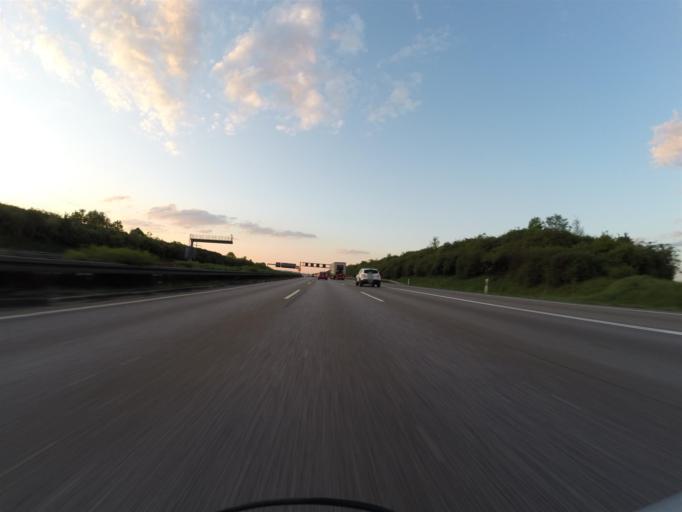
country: DE
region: Hesse
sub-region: Regierungsbezirk Darmstadt
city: Friedrichsdorf
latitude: 50.2173
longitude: 8.6632
